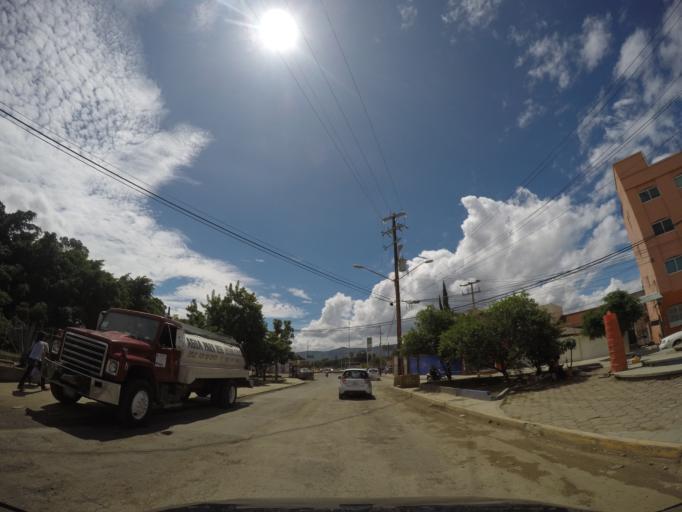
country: MX
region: Oaxaca
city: Oaxaca de Juarez
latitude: 17.0497
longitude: -96.7319
